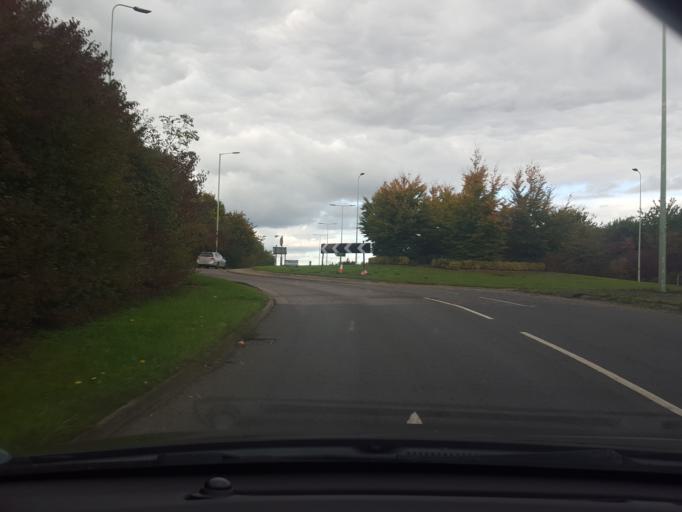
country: GB
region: England
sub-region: Suffolk
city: Bury St Edmunds
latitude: 52.2639
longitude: 0.7251
